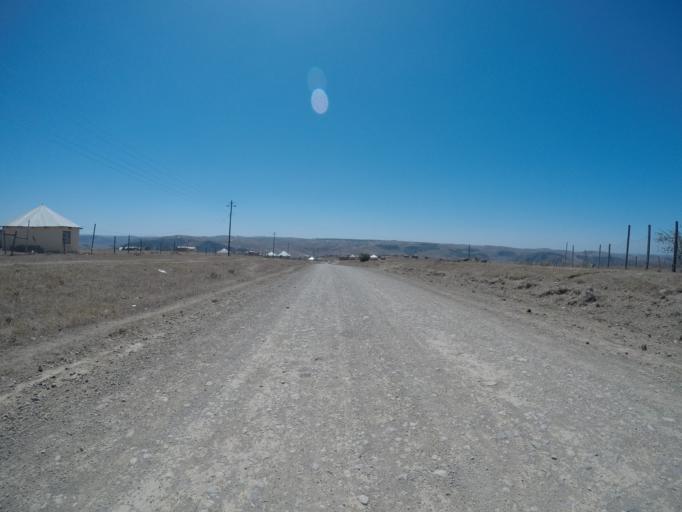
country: ZA
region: Eastern Cape
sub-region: OR Tambo District Municipality
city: Mthatha
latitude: -31.8822
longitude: 28.8749
